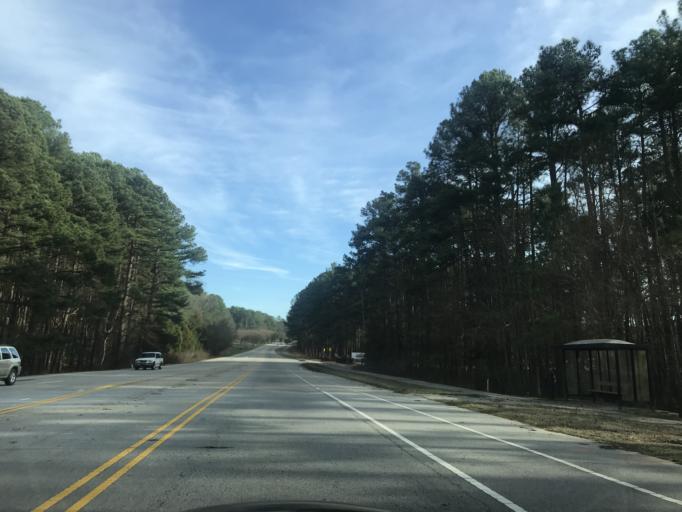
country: US
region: North Carolina
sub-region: Durham County
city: Durham
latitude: 35.9191
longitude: -78.8728
